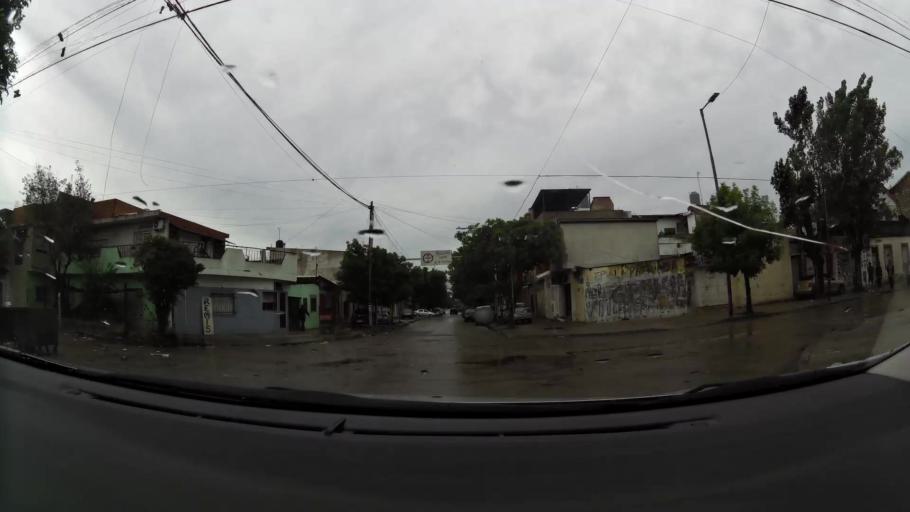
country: AR
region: Buenos Aires F.D.
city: Villa Lugano
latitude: -34.6606
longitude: -58.4509
